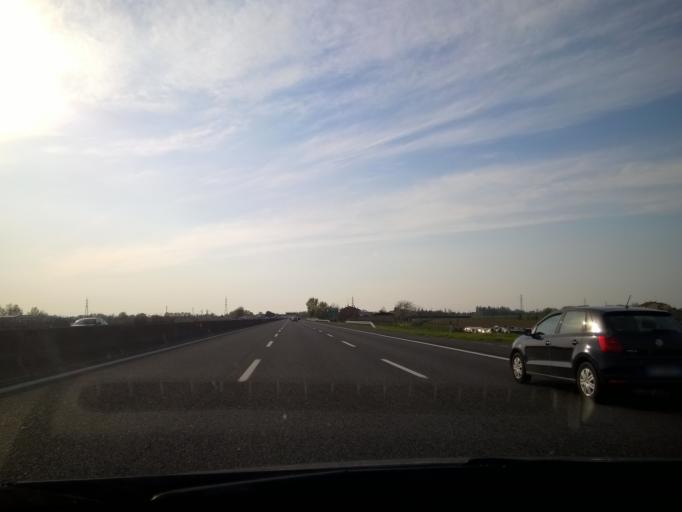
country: IT
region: Emilia-Romagna
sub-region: Forli-Cesena
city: Forlimpopoli
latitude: 44.2459
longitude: 12.1121
